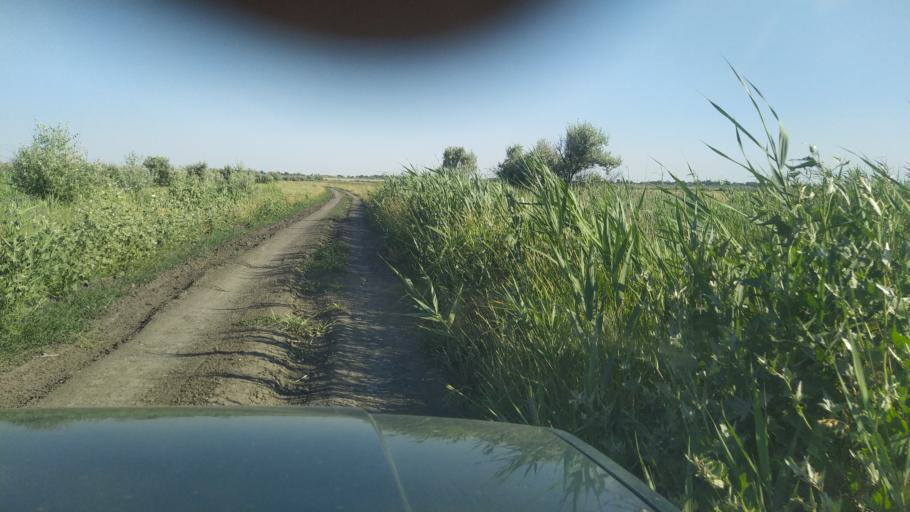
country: RU
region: Rostov
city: Kuleshovka
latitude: 47.1250
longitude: 39.6468
